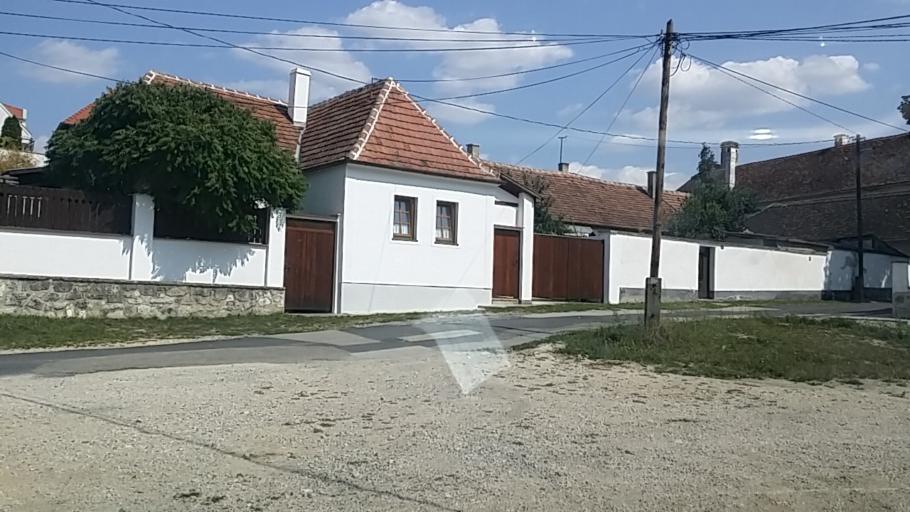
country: HU
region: Gyor-Moson-Sopron
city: Fertorakos
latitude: 47.7170
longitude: 16.6521
